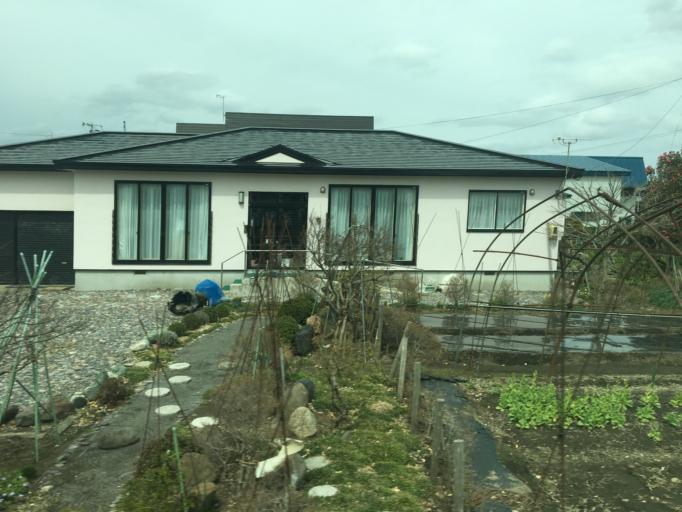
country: JP
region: Aomori
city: Shimokizukuri
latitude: 40.8070
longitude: 140.4062
